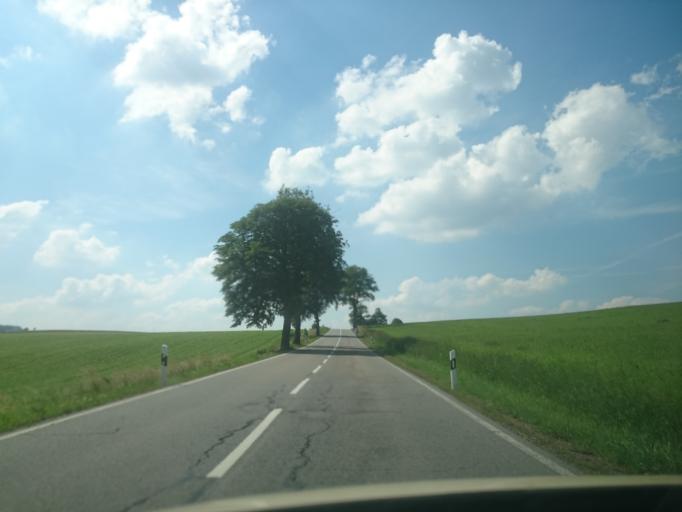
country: DE
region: Saxony
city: Lengefeld
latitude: 50.7125
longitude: 13.2056
